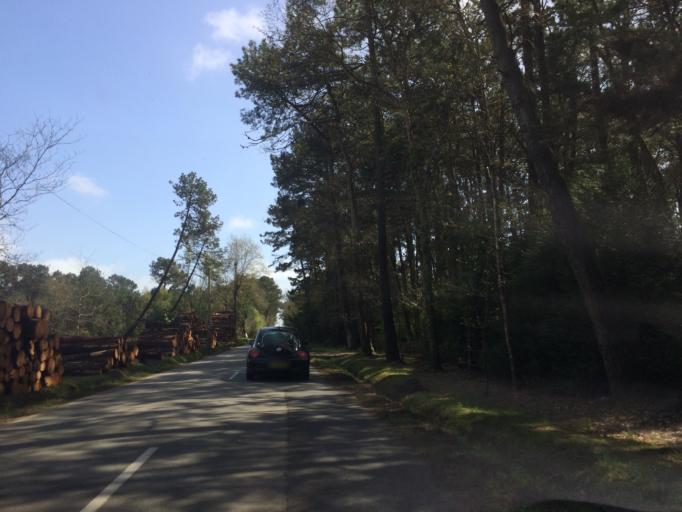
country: FR
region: Brittany
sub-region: Departement du Morbihan
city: La Trinite-sur-Mer
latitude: 47.6121
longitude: -3.0505
